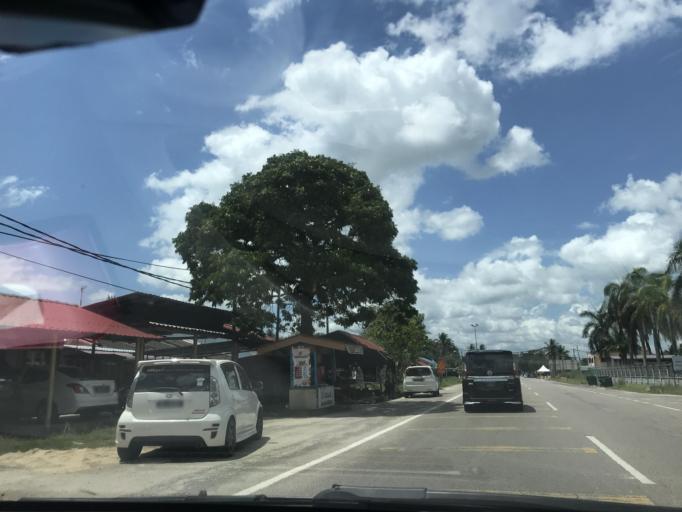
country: TH
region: Narathiwat
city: Tak Bai
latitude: 6.2279
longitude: 102.0955
